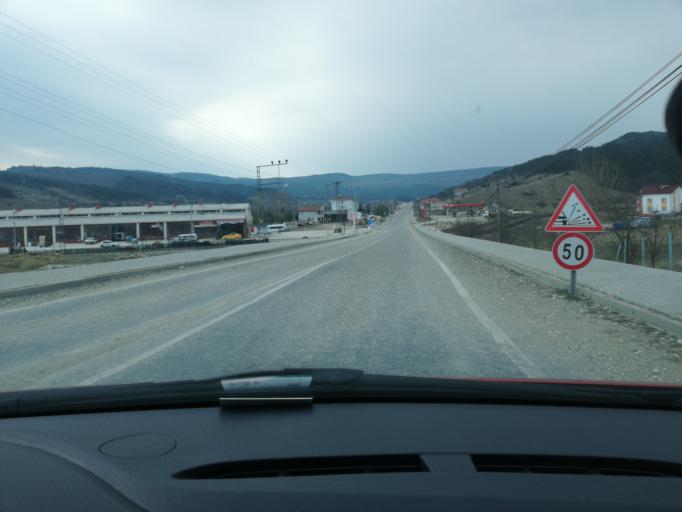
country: TR
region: Kastamonu
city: Pinarbasi
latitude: 41.6010
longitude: 33.1064
